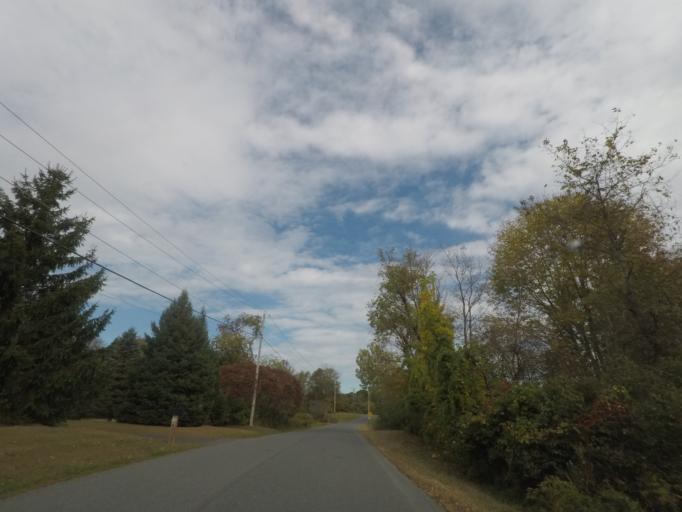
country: US
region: New York
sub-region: Rensselaer County
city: Nassau
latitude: 42.5528
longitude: -73.6409
